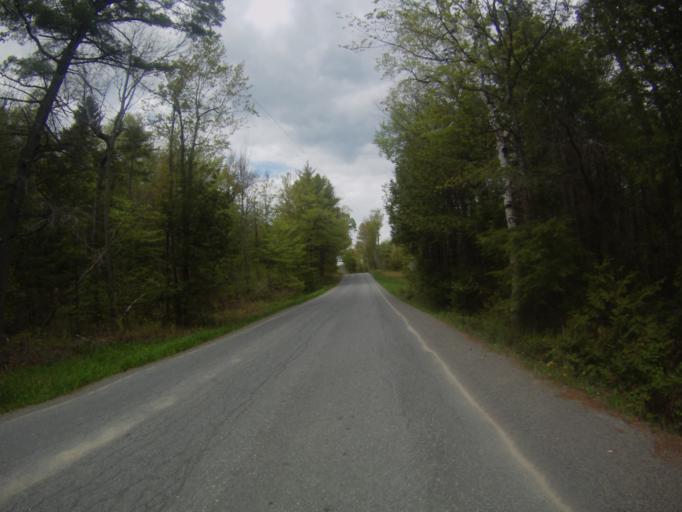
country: US
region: New York
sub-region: Essex County
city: Ticonderoga
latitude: 43.9218
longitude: -73.5036
